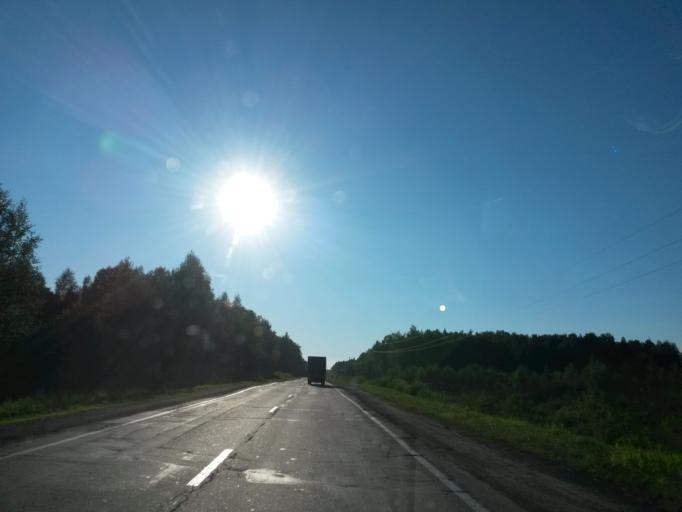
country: RU
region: Jaroslavl
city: Dubki
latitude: 57.2589
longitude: 40.0688
